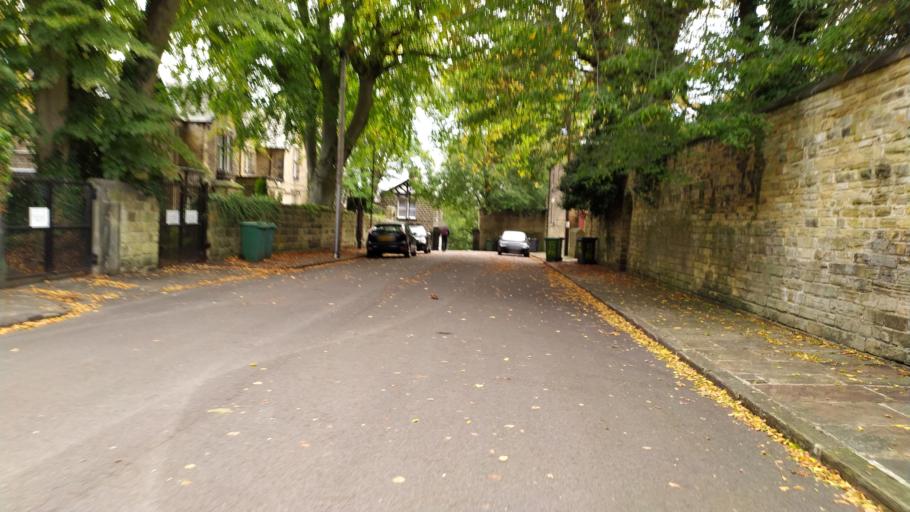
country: GB
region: England
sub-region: City and Borough of Leeds
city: Chapel Allerton
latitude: 53.8191
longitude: -1.5641
